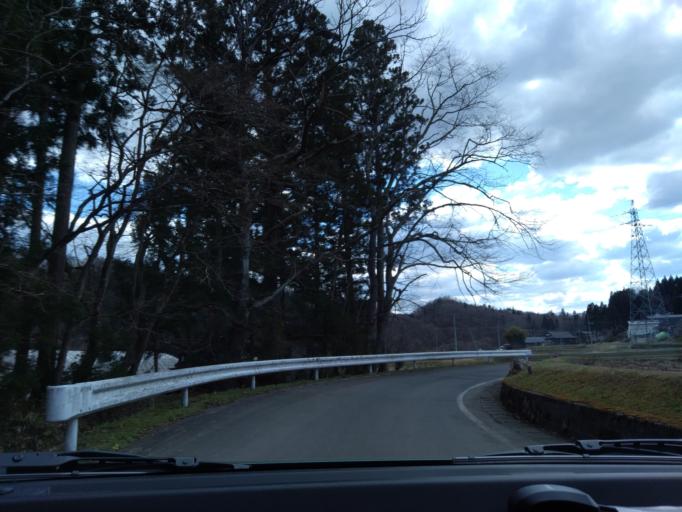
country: JP
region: Iwate
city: Ichinoseki
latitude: 38.9728
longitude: 141.0765
